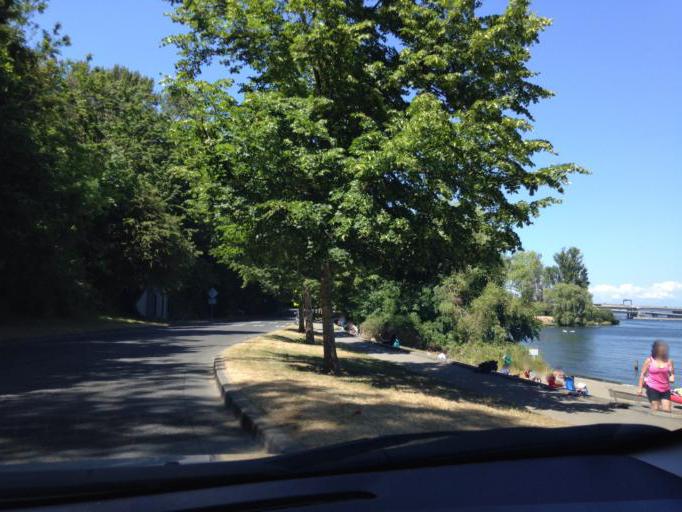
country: US
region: Washington
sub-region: King County
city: Seattle
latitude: 47.5831
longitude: -122.2879
